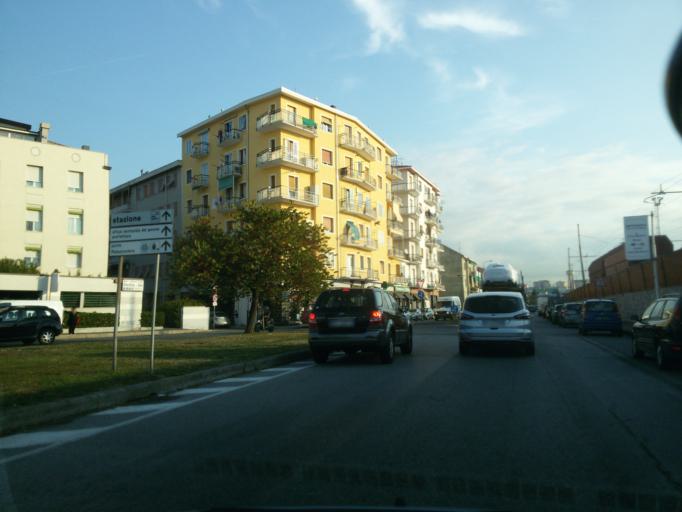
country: IT
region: Liguria
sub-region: Provincia di Savona
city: Valleggia
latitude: 44.2941
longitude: 8.4538
